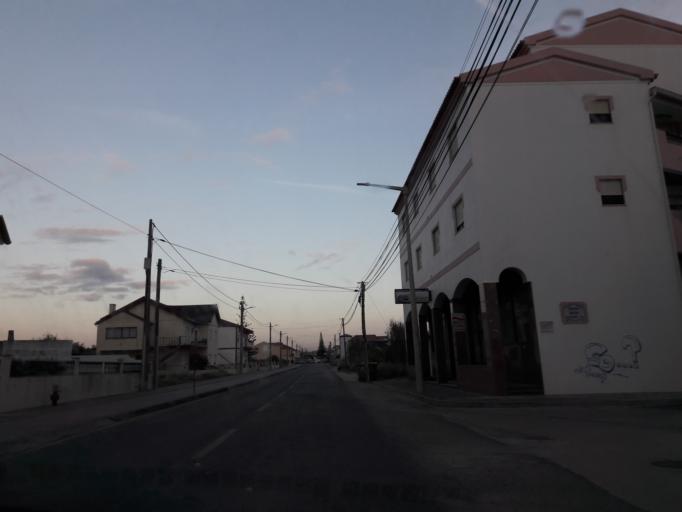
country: PT
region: Leiria
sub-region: Peniche
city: Atouguia da Baleia
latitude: 39.3673
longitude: -9.3236
